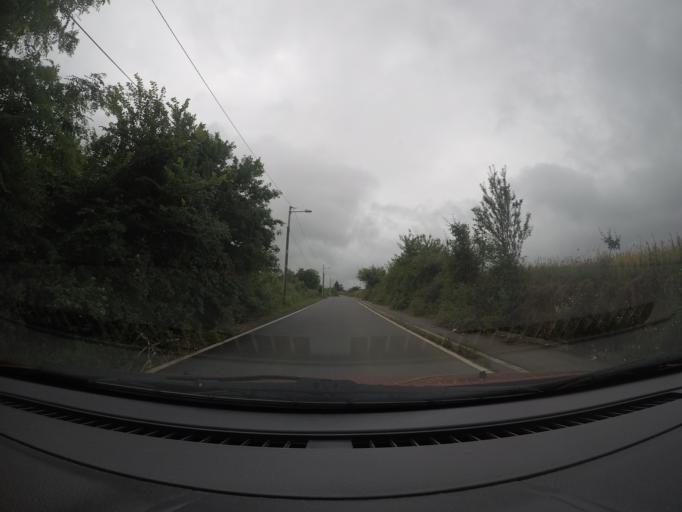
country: RS
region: Central Serbia
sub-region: Belgrade
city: Zvezdara
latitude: 44.7019
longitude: 20.5626
